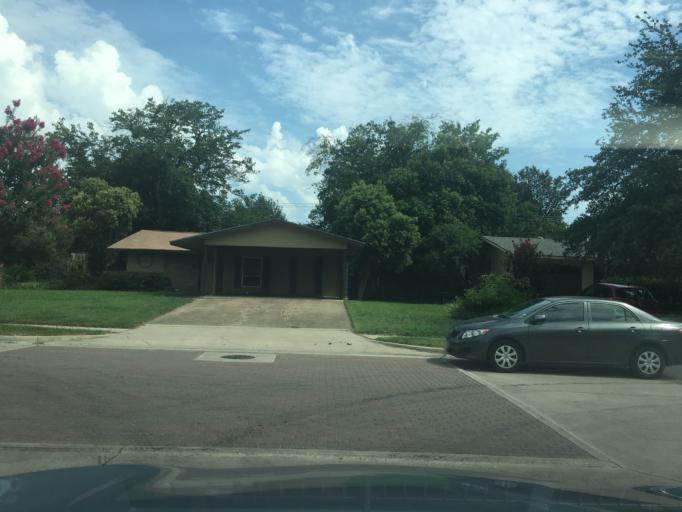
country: US
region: Texas
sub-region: Dallas County
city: Farmers Branch
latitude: 32.9303
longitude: -96.8652
